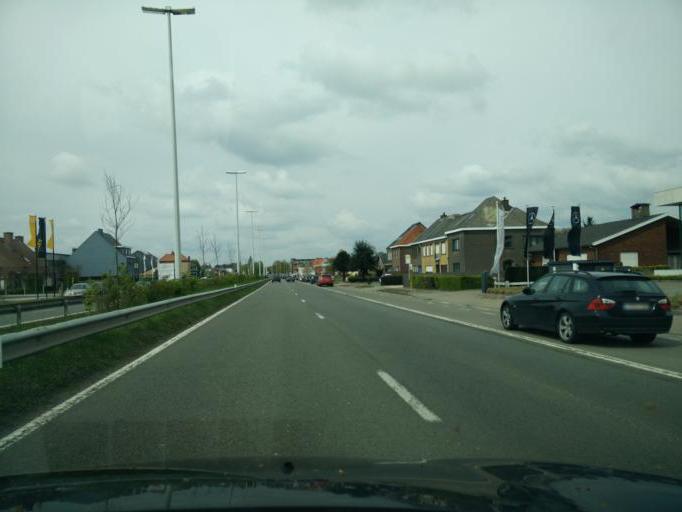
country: BE
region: Flanders
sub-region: Provincie Oost-Vlaanderen
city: Oudenaarde
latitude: 50.8241
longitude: 3.6039
